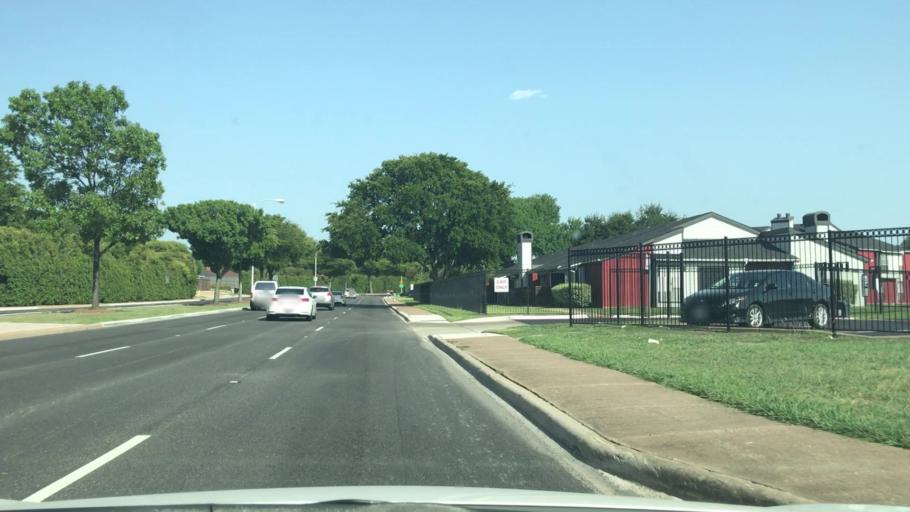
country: US
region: Texas
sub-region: Collin County
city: Plano
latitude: 33.0247
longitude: -96.7521
